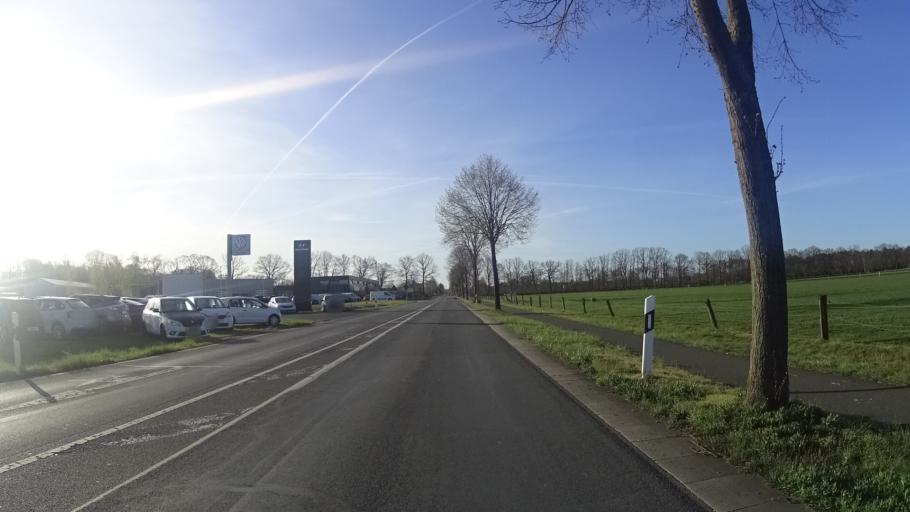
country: DE
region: North Rhine-Westphalia
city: Emsdetten
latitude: 52.1405
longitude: 7.5390
